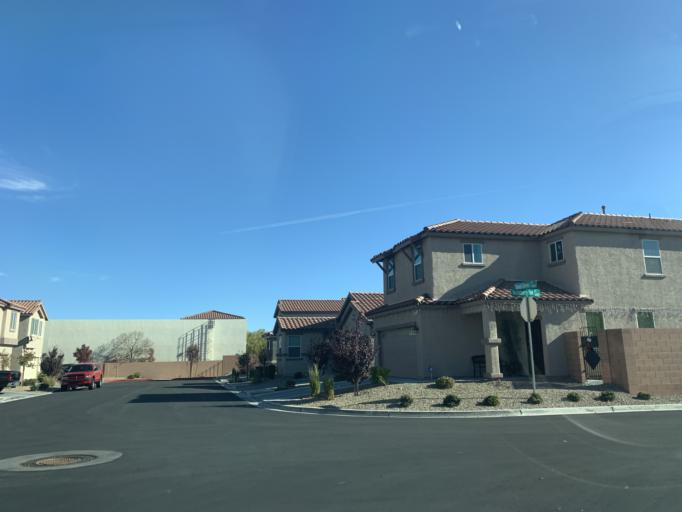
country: US
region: Nevada
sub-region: Clark County
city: Summerlin South
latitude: 36.1235
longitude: -115.2988
